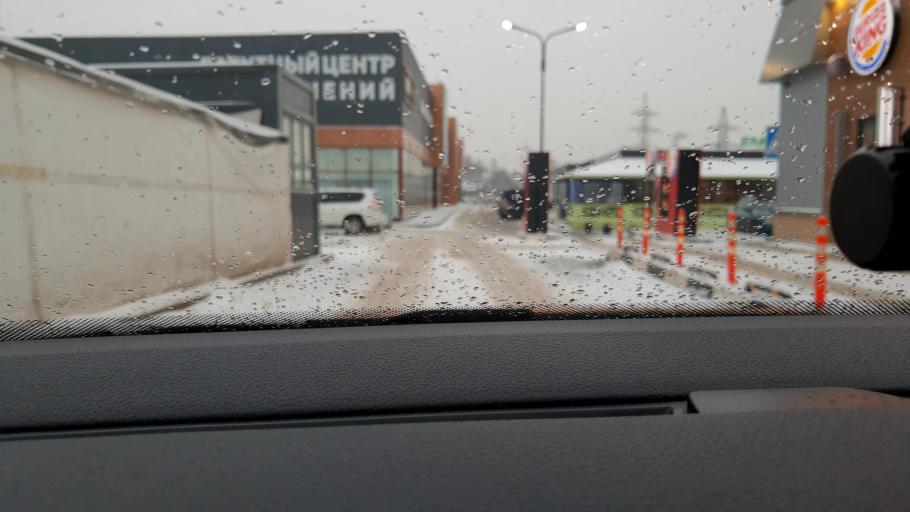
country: RU
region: Moskovskaya
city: Novopodrezkovo
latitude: 55.9378
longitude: 37.3222
